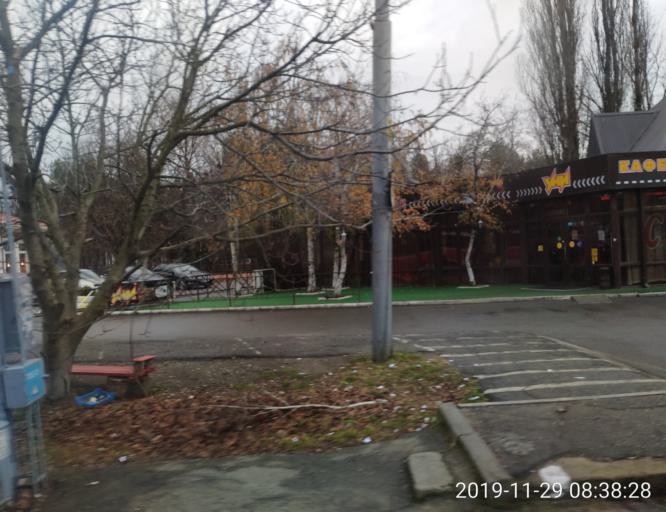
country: RU
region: Krasnodarskiy
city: Krasnodar
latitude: 45.0505
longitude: 39.0022
